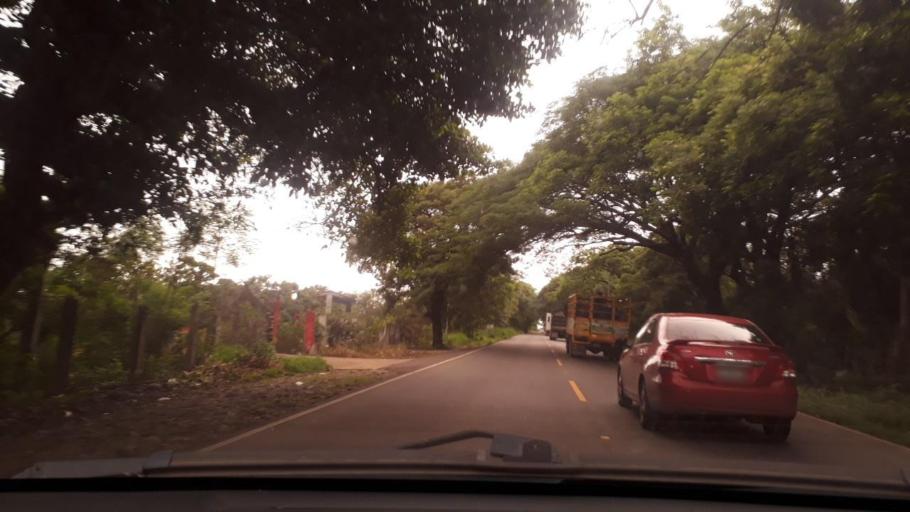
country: GT
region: Jutiapa
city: Asuncion Mita
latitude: 14.3527
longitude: -89.7643
